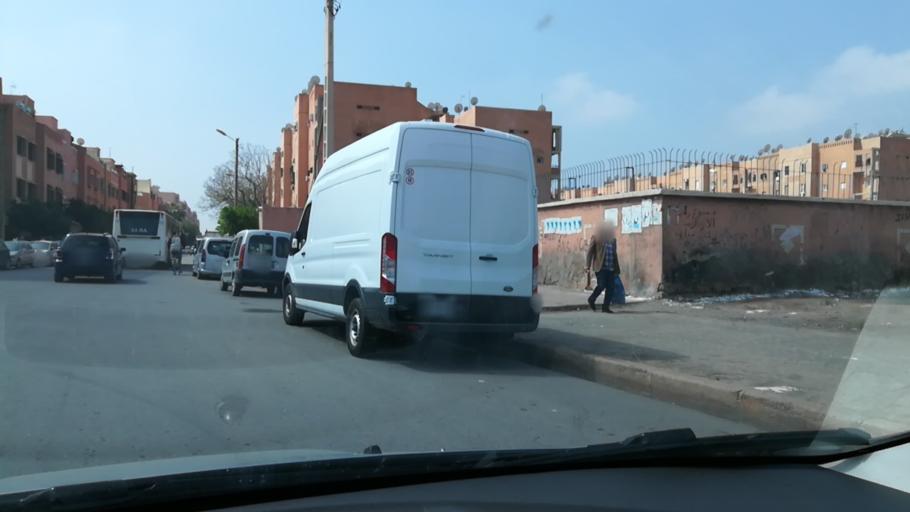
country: MA
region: Marrakech-Tensift-Al Haouz
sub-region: Marrakech
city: Marrakesh
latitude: 31.6339
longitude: -8.0625
